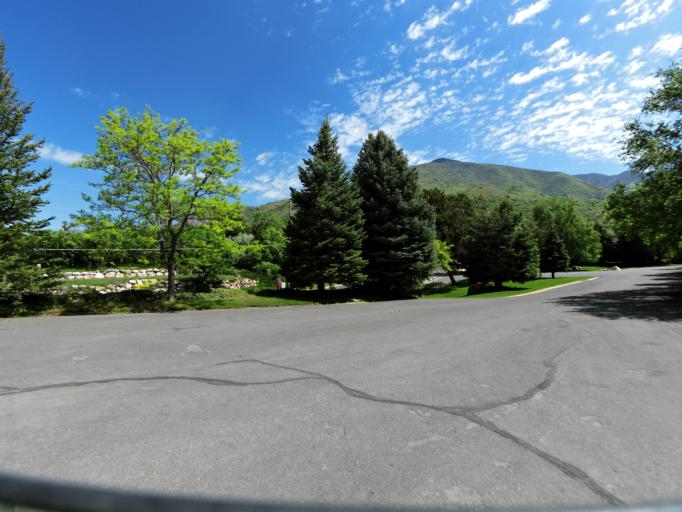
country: US
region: Utah
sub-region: Weber County
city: Uintah
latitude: 41.1782
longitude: -111.9366
